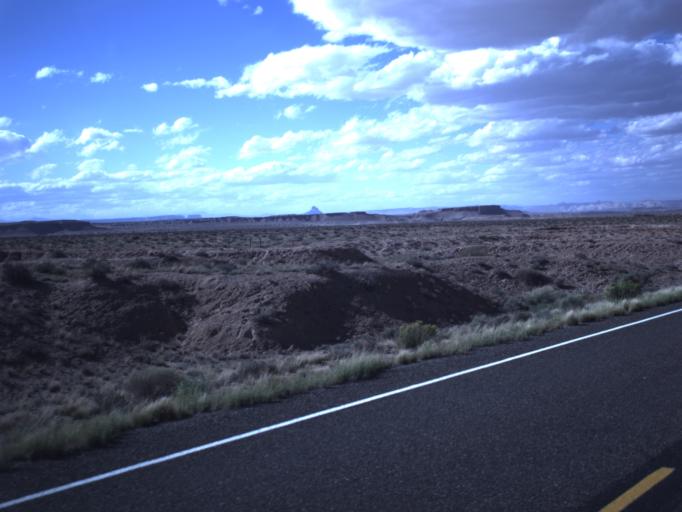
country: US
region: Utah
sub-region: Emery County
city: Ferron
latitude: 38.2920
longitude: -110.6661
